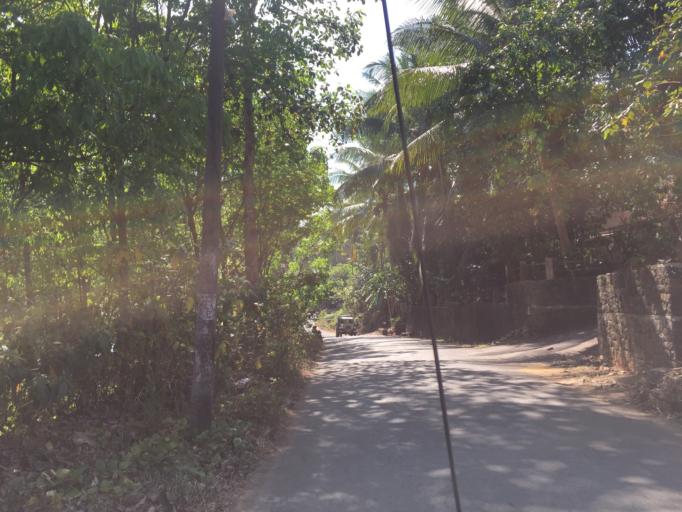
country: IN
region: Kerala
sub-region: Kottayam
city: Erattupetta
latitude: 9.6858
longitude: 76.7678
